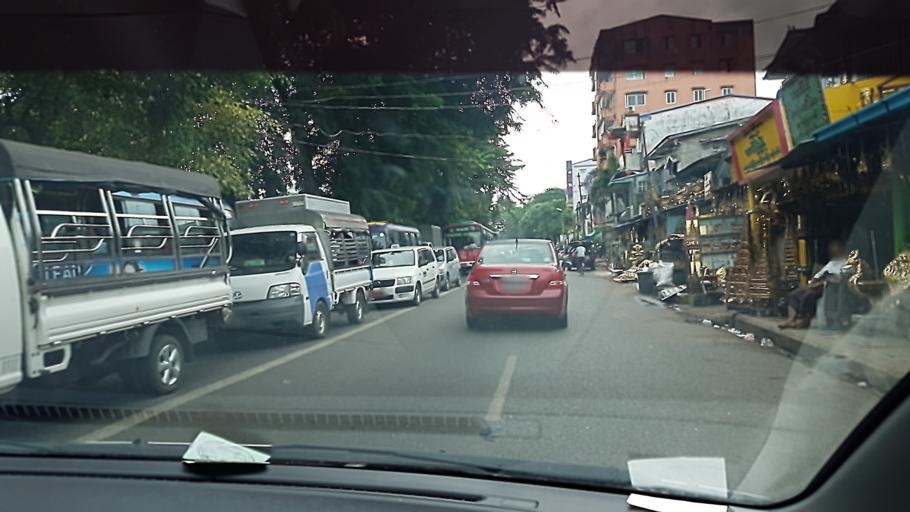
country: MM
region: Yangon
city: Yangon
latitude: 16.8026
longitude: 96.1260
